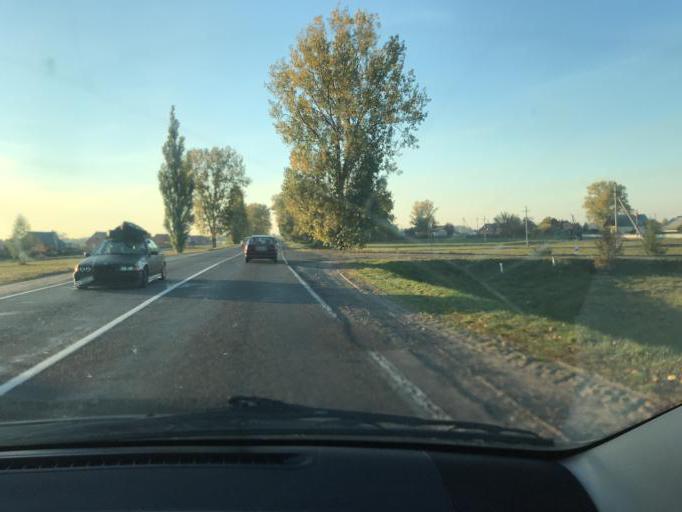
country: BY
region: Brest
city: Pinsk
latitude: 52.0650
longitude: 26.1945
